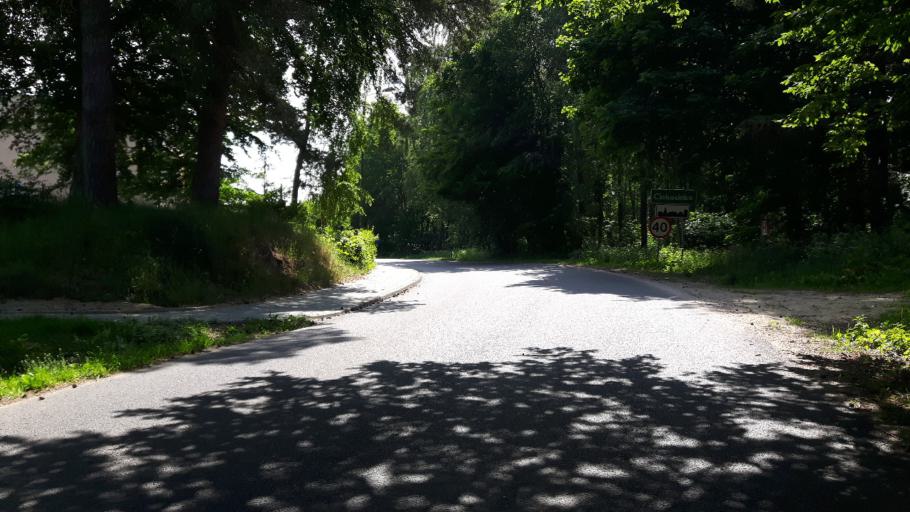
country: PL
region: Pomeranian Voivodeship
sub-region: Powiat wejherowski
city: Choczewo
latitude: 54.7478
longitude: 17.7956
